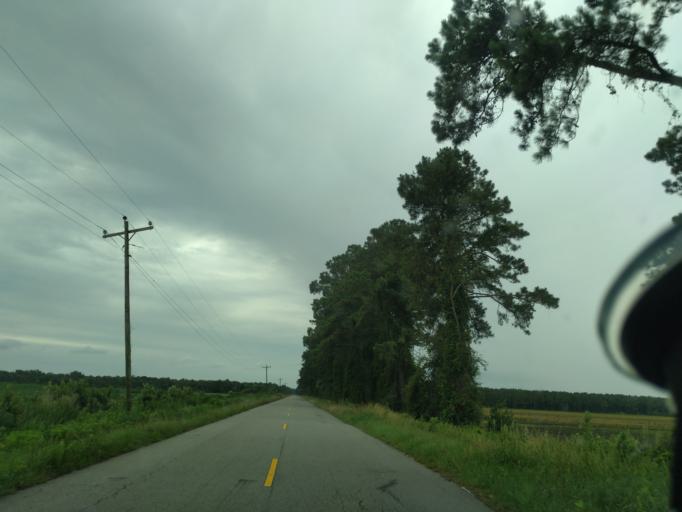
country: US
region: North Carolina
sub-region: Washington County
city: Plymouth
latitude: 35.8104
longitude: -76.5159
